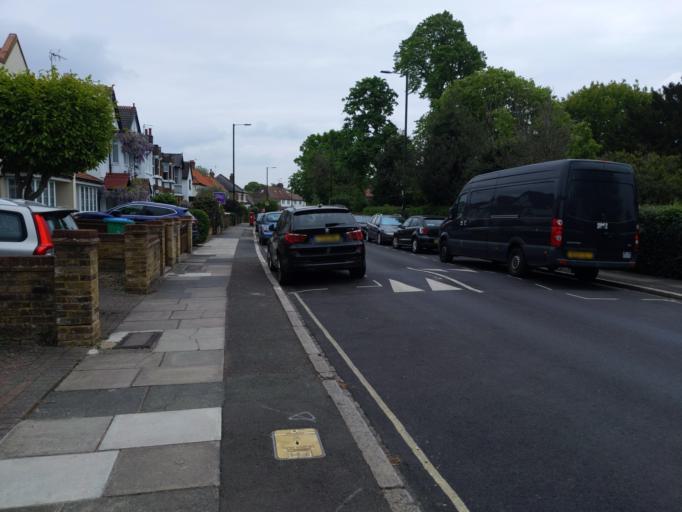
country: GB
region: England
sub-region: Greater London
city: Hounslow
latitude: 51.4563
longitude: -0.3600
